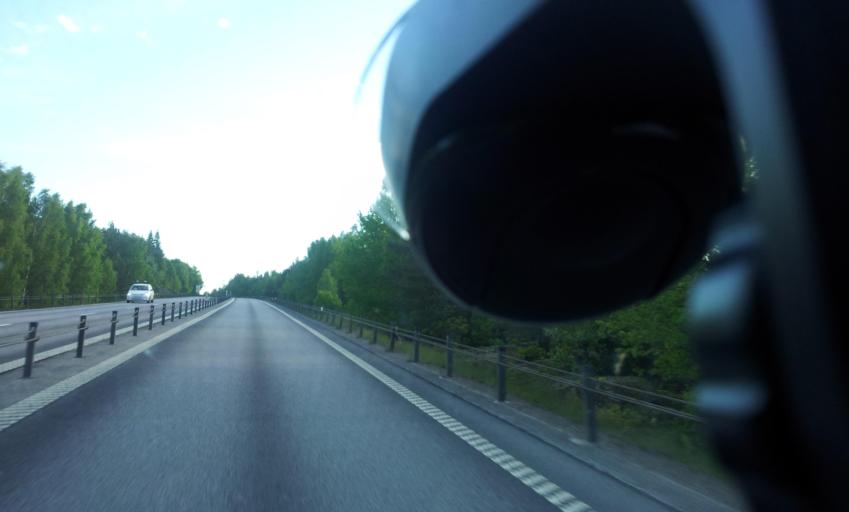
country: SE
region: Kalmar
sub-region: Oskarshamns Kommun
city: Oskarshamn
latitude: 57.2892
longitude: 16.4567
